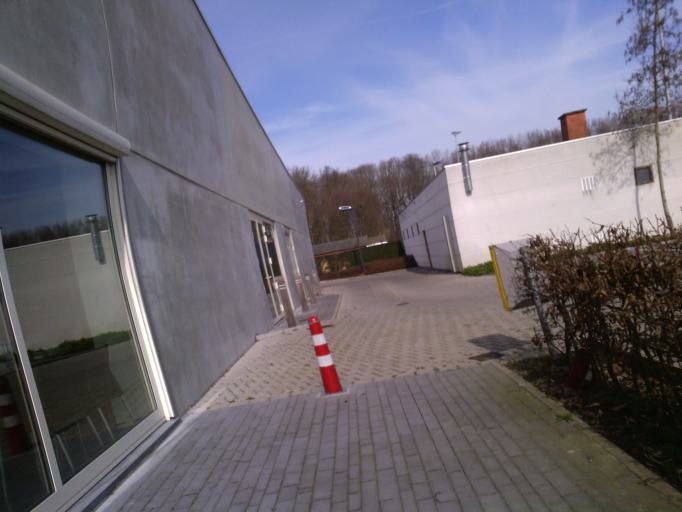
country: BE
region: Flanders
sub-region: Provincie West-Vlaanderen
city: Ieper
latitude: 50.8811
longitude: 2.8164
